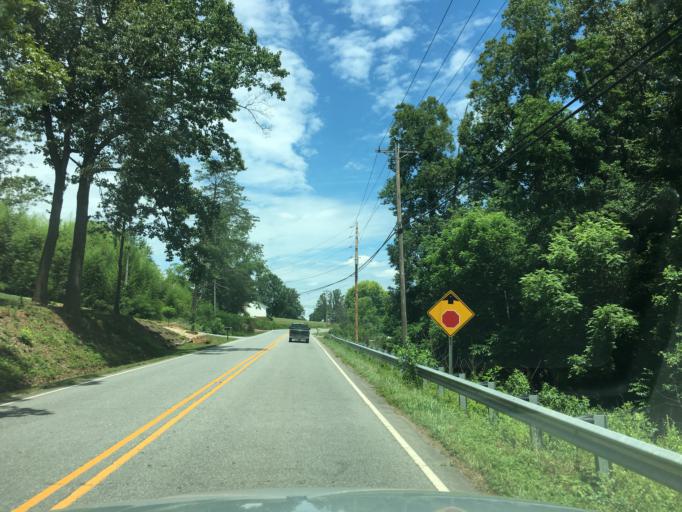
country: US
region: North Carolina
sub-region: Burke County
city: Glen Alpine
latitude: 35.7107
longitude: -81.7632
